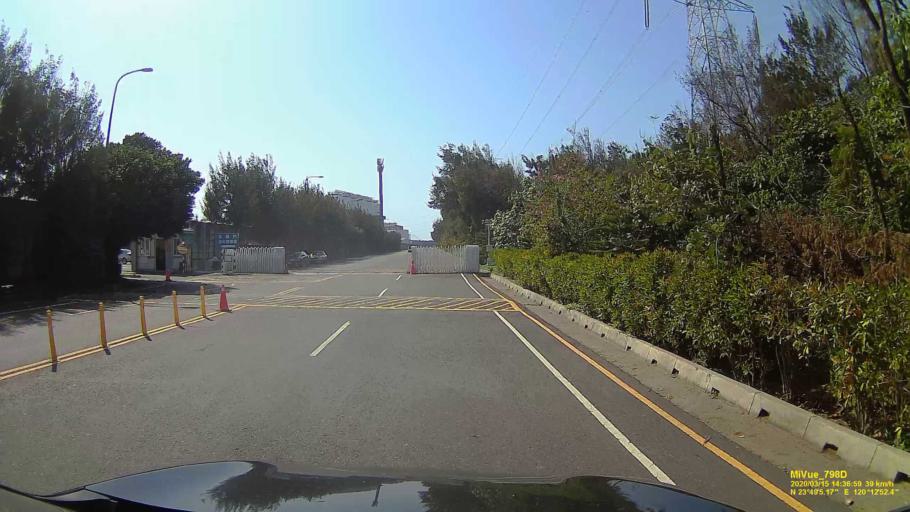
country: TW
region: Taiwan
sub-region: Yunlin
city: Douliu
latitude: 23.8181
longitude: 120.2144
